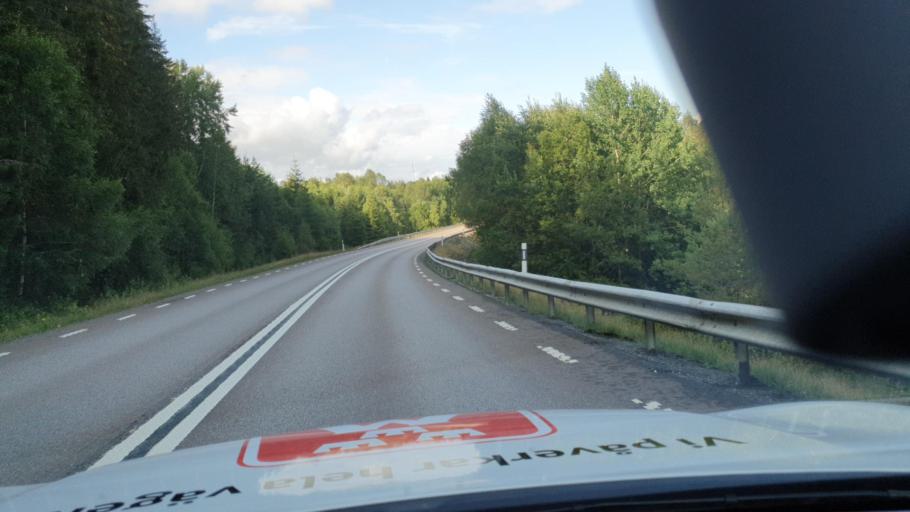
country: SE
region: Vaestra Goetaland
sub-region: Dals-Ed Kommun
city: Ed
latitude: 58.9327
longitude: 12.0438
